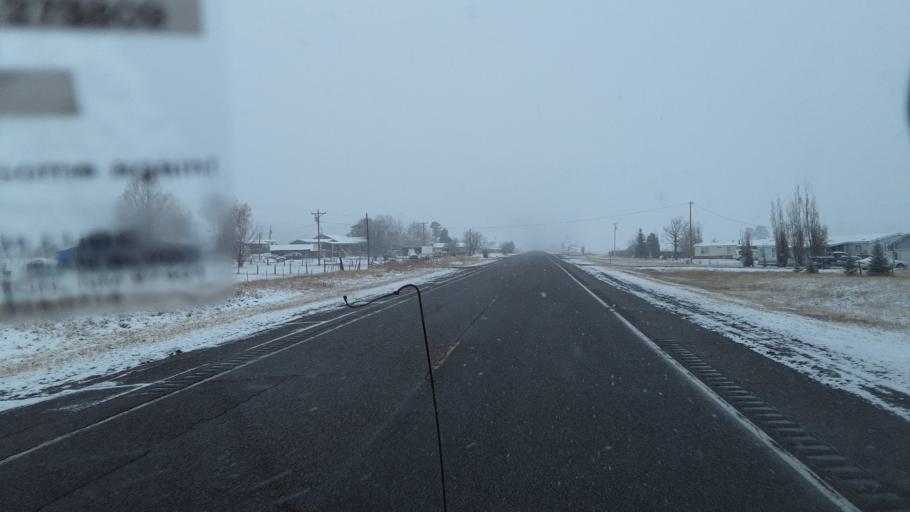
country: US
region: New Mexico
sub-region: Rio Arriba County
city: Chama
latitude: 36.8851
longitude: -106.6104
